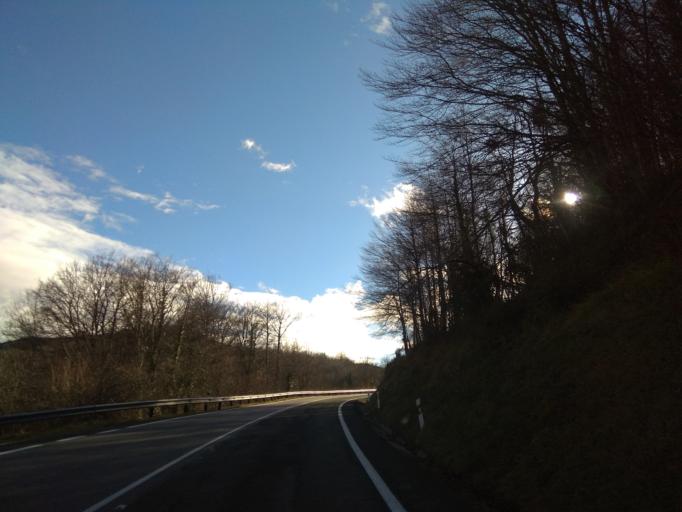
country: ES
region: Cantabria
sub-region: Provincia de Cantabria
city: San Martin de Elines
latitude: 42.9393
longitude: -3.8296
